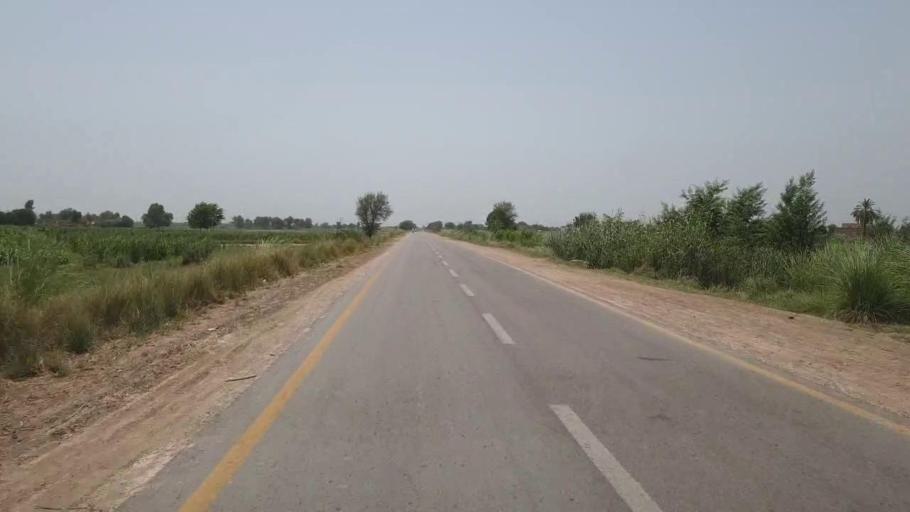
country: PK
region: Sindh
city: Moro
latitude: 26.6048
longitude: 68.0536
